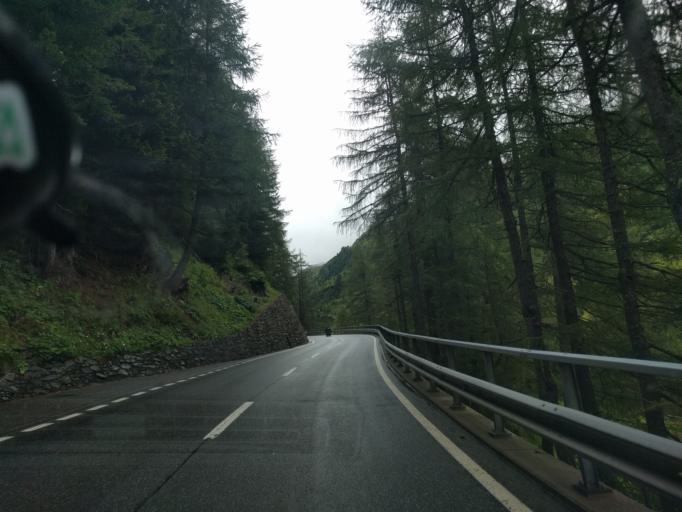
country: CH
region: Grisons
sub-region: Praettigau/Davos District
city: Davos
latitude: 46.7969
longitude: 9.9044
